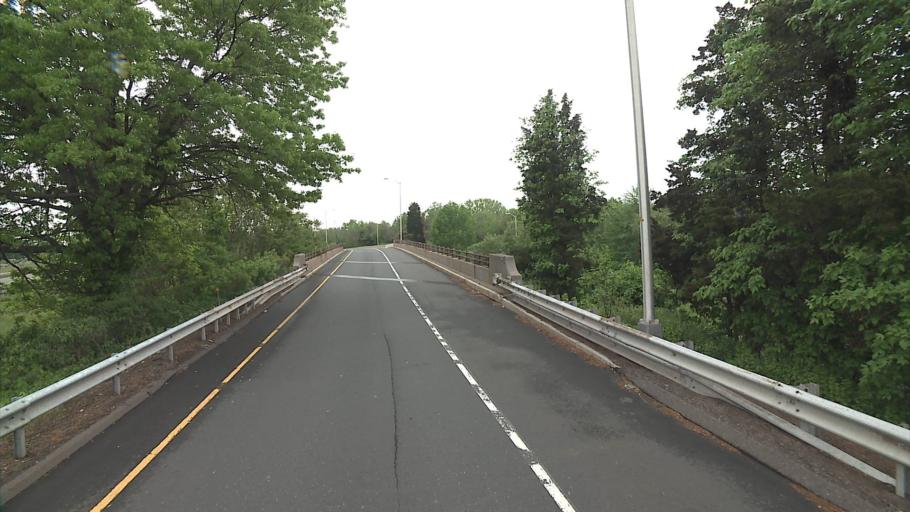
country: US
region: Connecticut
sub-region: New Haven County
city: Meriden
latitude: 41.5328
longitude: -72.7689
